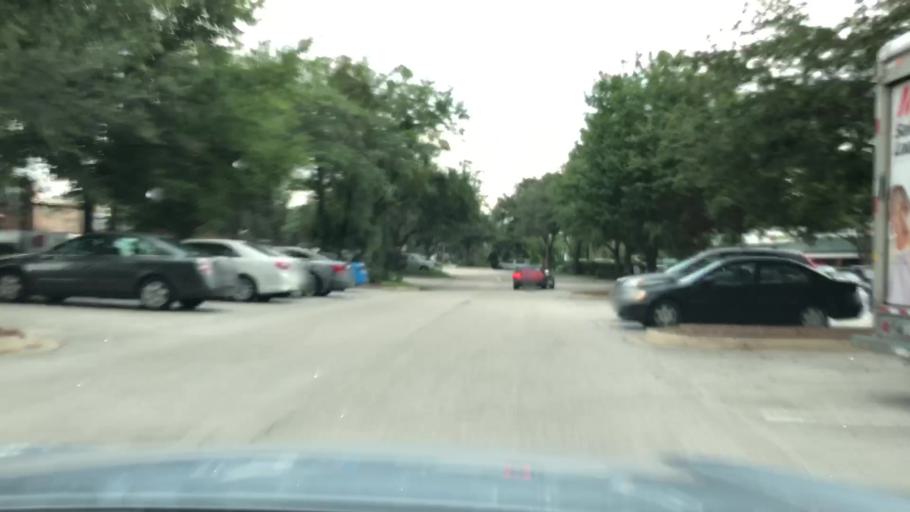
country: US
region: Florida
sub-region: Duval County
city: Jacksonville
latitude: 30.2634
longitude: -81.5559
